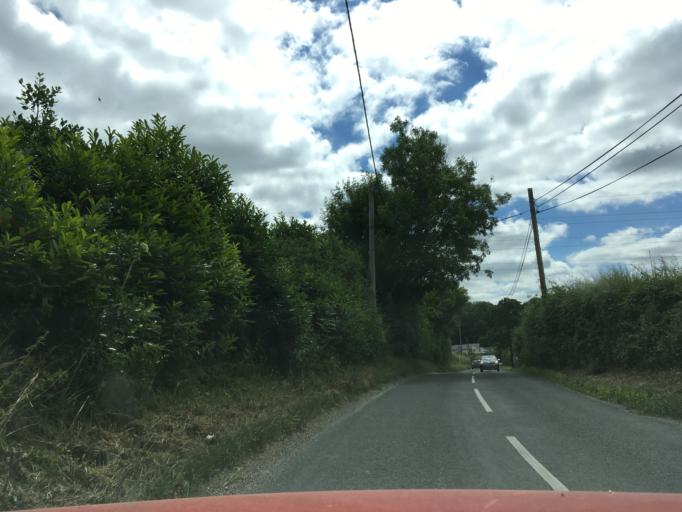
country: GB
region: England
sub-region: Hampshire
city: Highclere
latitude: 51.2414
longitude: -1.3851
